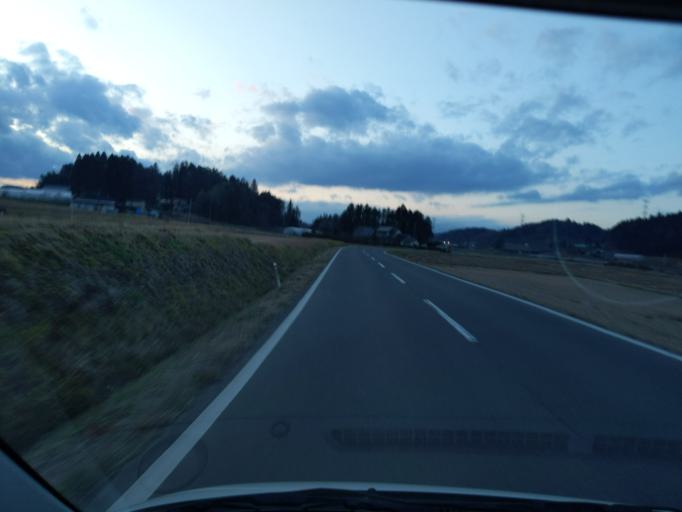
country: JP
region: Iwate
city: Ichinoseki
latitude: 38.8476
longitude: 141.1057
